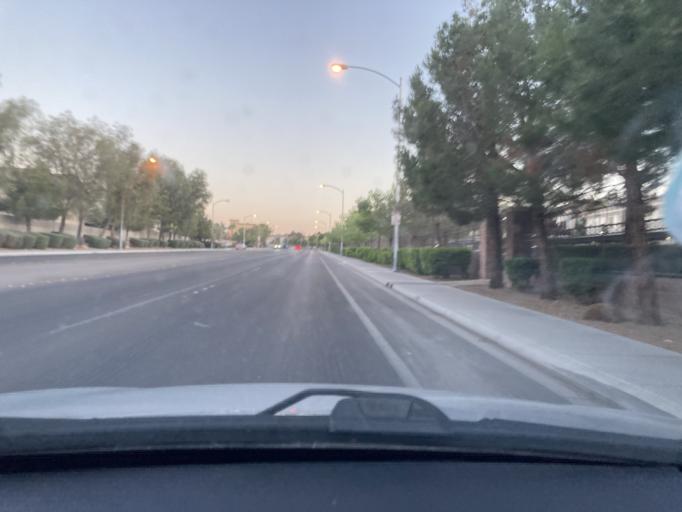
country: US
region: Nevada
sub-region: Clark County
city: Enterprise
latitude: 36.0580
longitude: -115.2882
